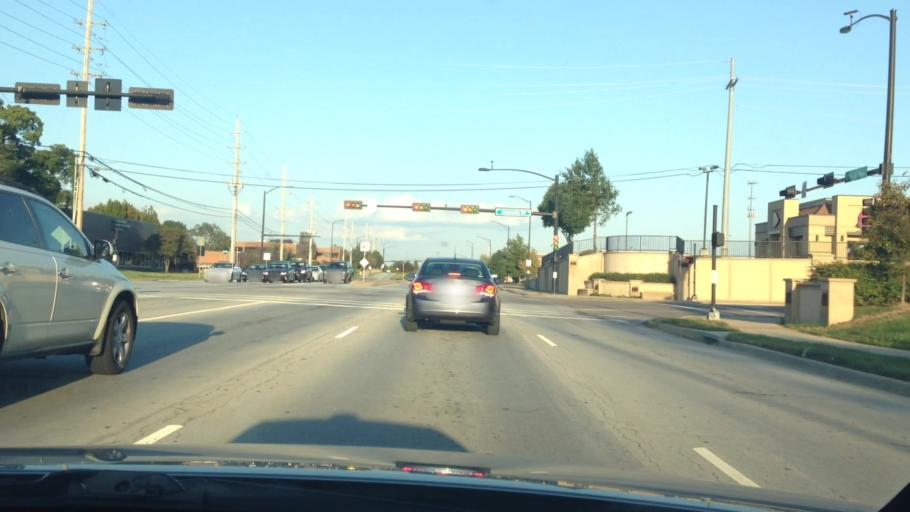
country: US
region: Kansas
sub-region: Johnson County
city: Lenexa
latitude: 38.9710
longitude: -94.7290
